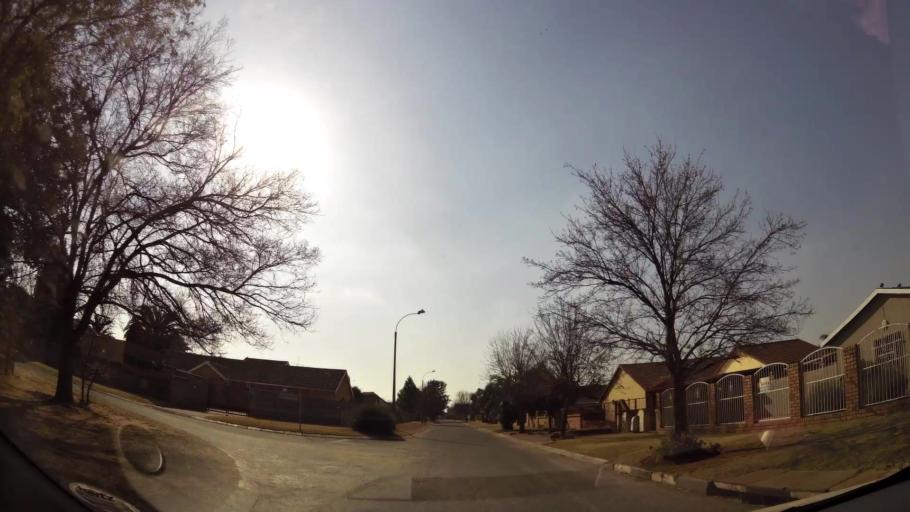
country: ZA
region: Gauteng
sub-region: West Rand District Municipality
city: Randfontein
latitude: -26.1844
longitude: 27.6798
